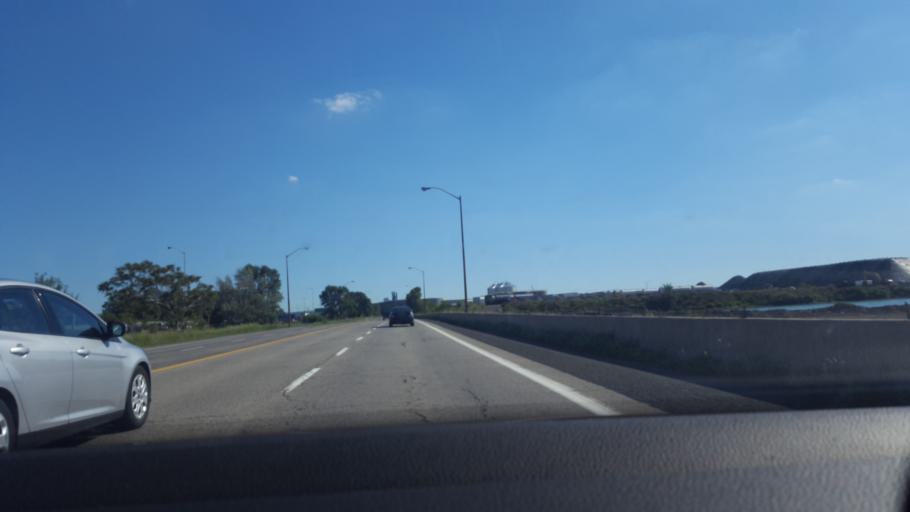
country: CA
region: Ontario
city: Hamilton
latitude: 43.2836
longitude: -79.7895
